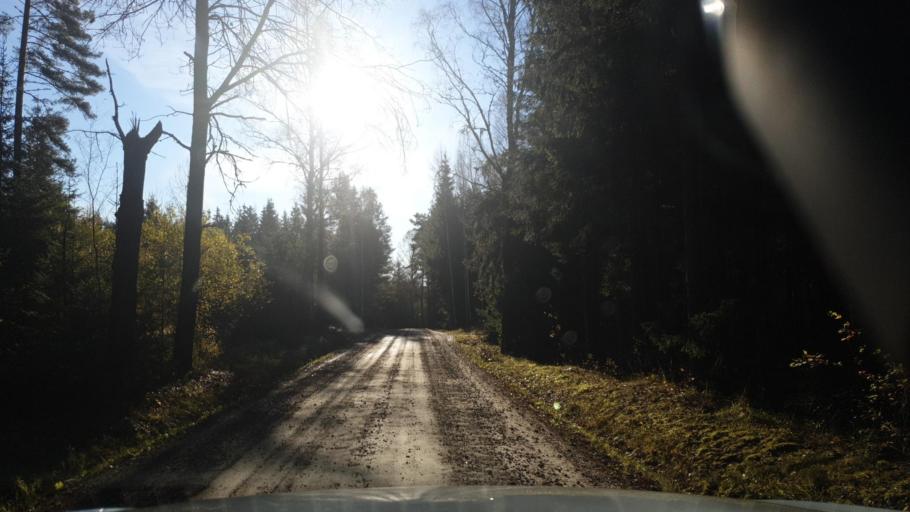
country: SE
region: Vaermland
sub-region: Karlstads Kommun
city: Edsvalla
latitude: 59.5167
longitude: 13.0108
